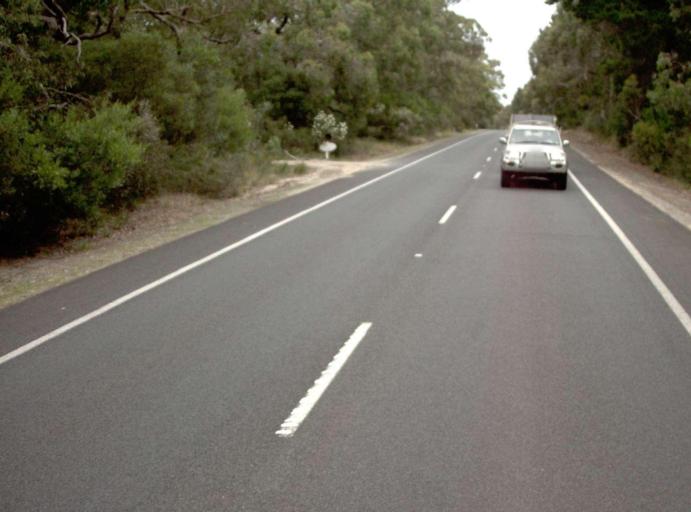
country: AU
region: Victoria
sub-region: Wellington
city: Sale
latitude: -38.1878
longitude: 147.0804
